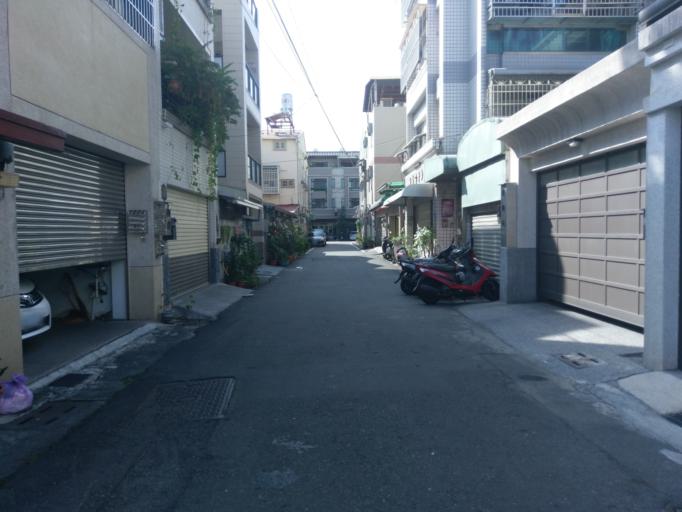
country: TW
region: Taiwan
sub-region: Yunlin
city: Douliu
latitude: 23.7126
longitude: 120.5491
